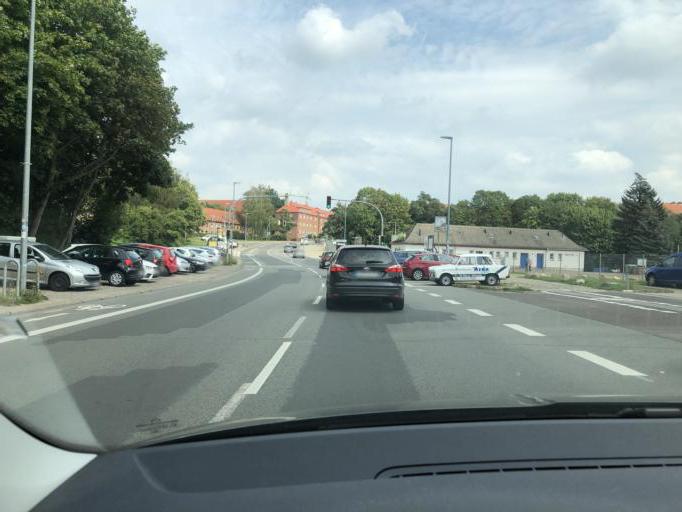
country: DE
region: Mecklenburg-Vorpommern
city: Weststadt
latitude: 53.6285
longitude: 11.3936
